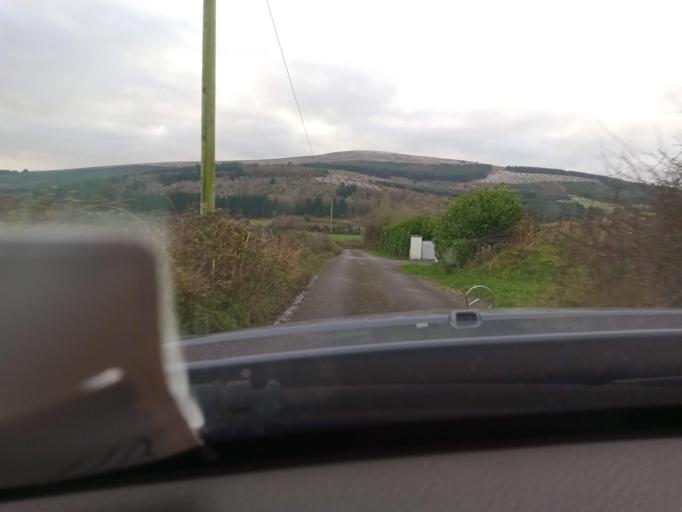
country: IE
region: Leinster
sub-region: Kilkenny
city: Graiguenamanagh
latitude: 52.5213
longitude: -6.9450
